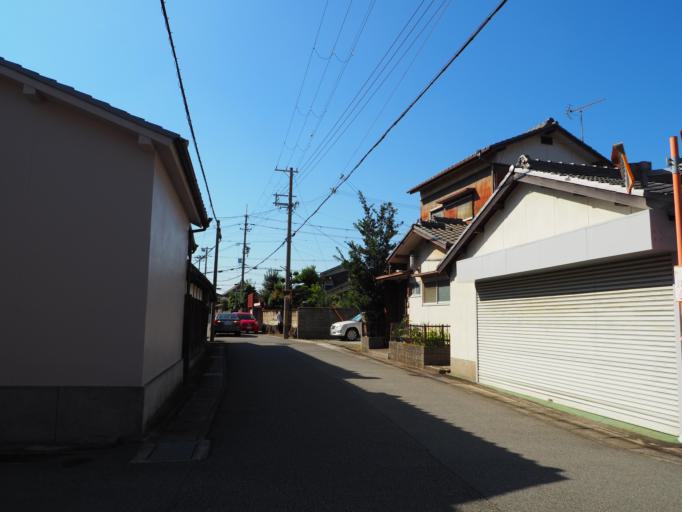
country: JP
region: Hyogo
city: Himeji
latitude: 34.8019
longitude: 134.6428
